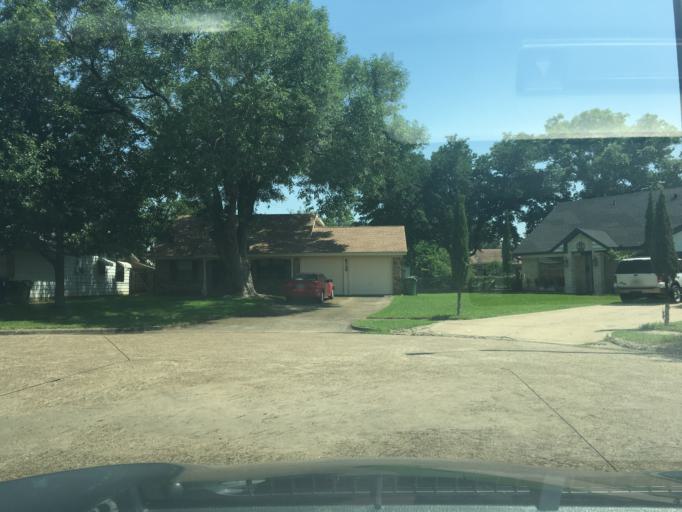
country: US
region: Texas
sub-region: Dallas County
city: Richardson
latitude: 32.9251
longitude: -96.7052
